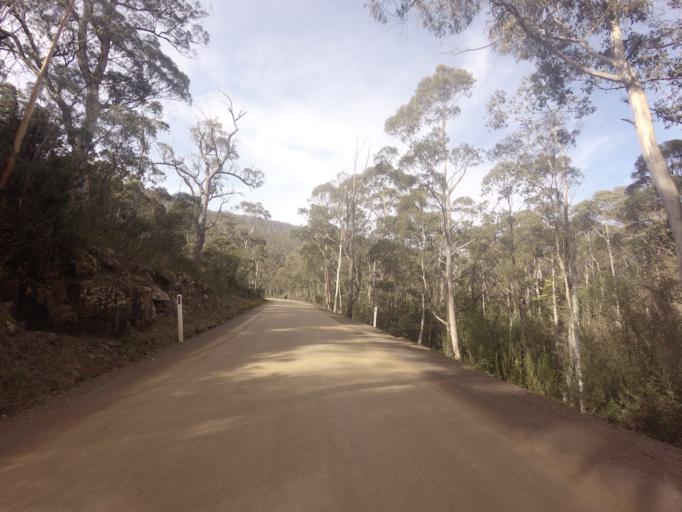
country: AU
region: Tasmania
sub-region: Huon Valley
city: Huonville
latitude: -43.0626
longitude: 147.0903
